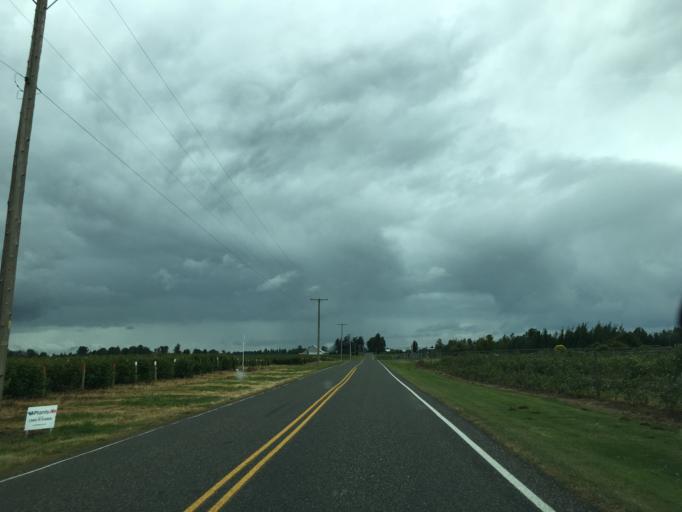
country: US
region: Washington
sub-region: Whatcom County
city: Everson
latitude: 48.9819
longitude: -122.3551
